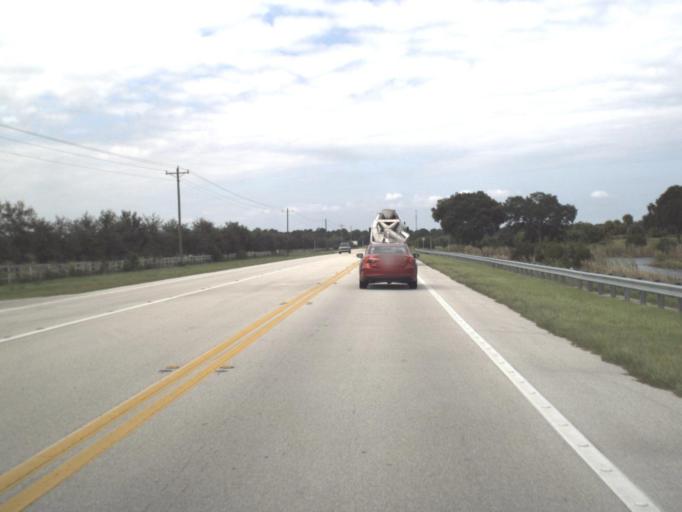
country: US
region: Florida
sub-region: Glades County
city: Moore Haven
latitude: 26.7684
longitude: -81.2279
